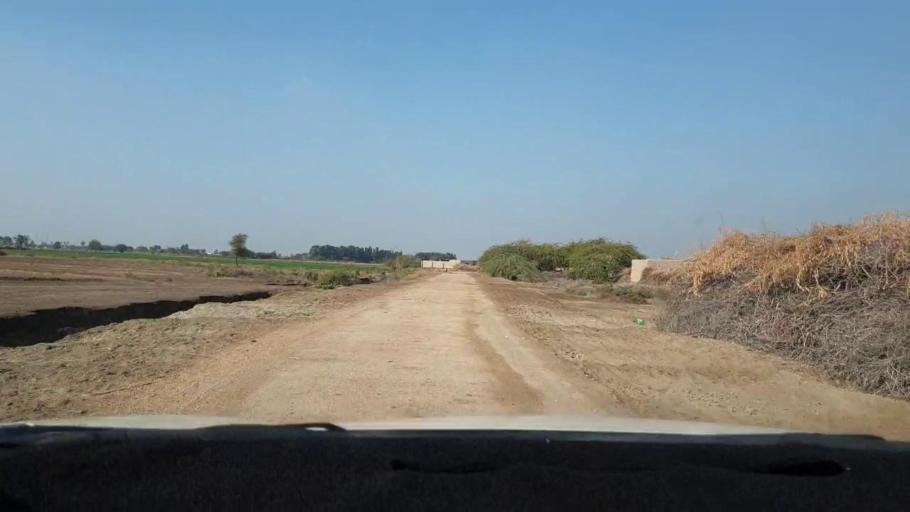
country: PK
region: Sindh
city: Berani
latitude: 25.7731
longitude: 68.8282
